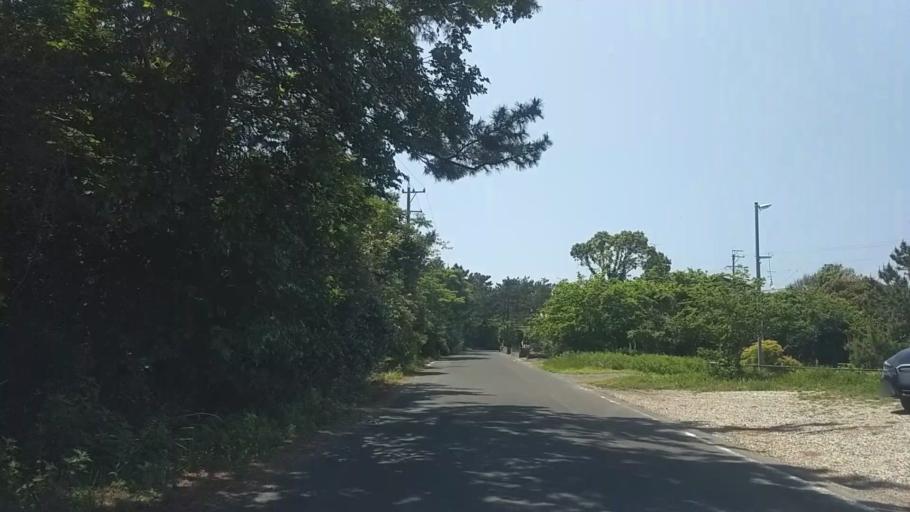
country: JP
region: Shizuoka
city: Kosai-shi
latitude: 34.6825
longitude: 137.5842
